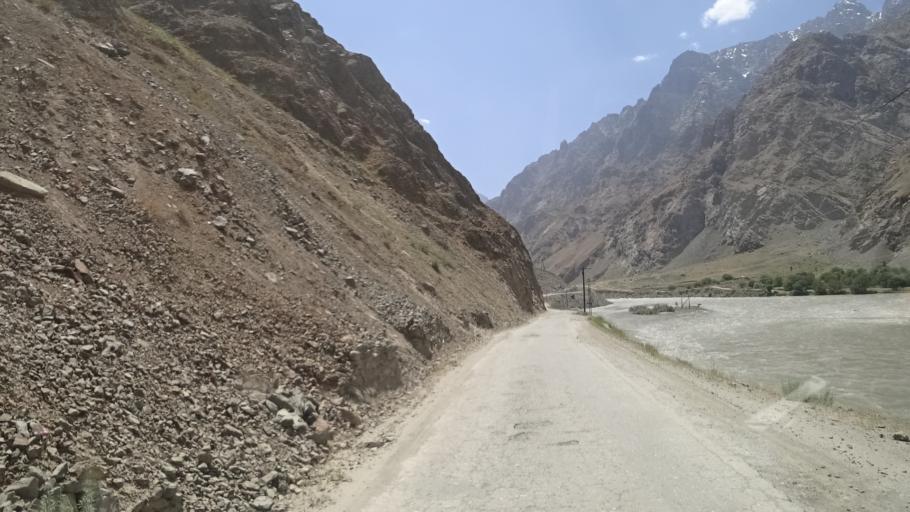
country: TJ
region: Gorno-Badakhshan
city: Rushon
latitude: 37.8497
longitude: 71.5876
